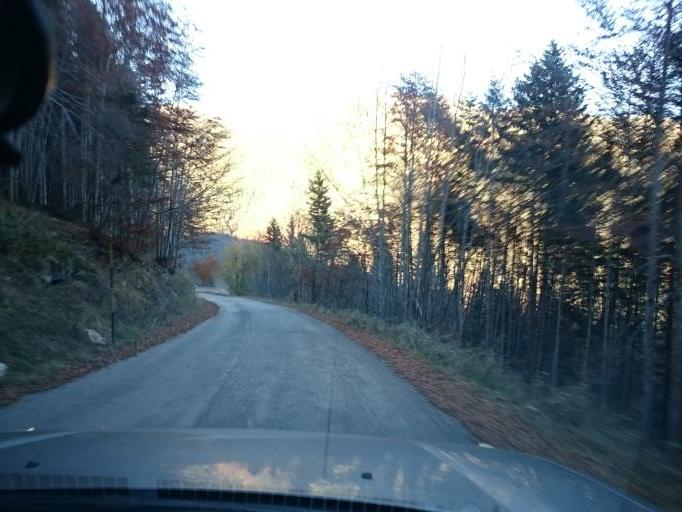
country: IT
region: Trentino-Alto Adige
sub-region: Provincia di Trento
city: Novaledo
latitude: 45.9586
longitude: 11.4218
